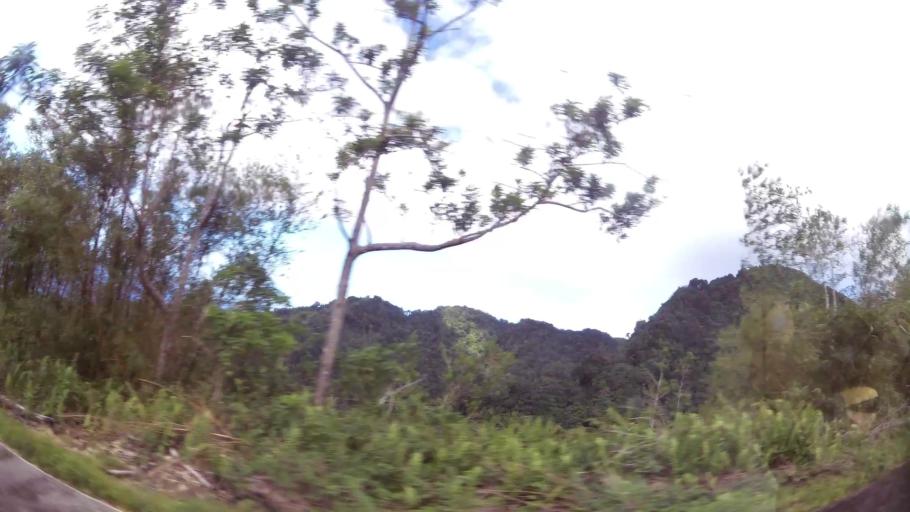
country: DM
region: Saint John
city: Portsmouth
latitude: 15.6148
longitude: -61.4455
